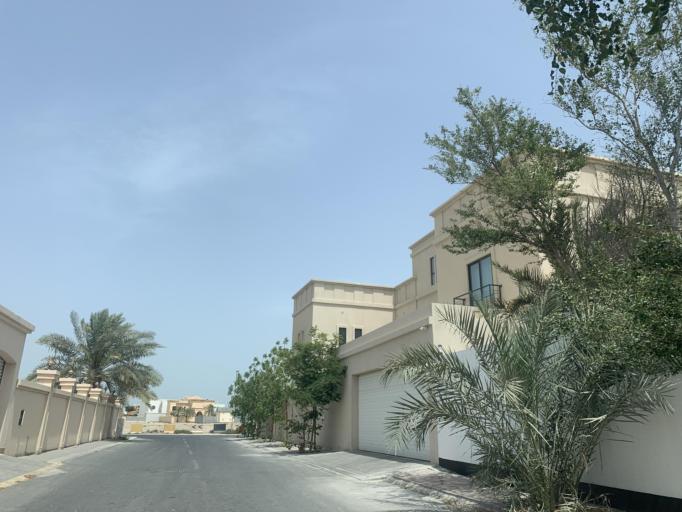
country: BH
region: Northern
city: Madinat `Isa
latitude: 26.1583
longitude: 50.5591
